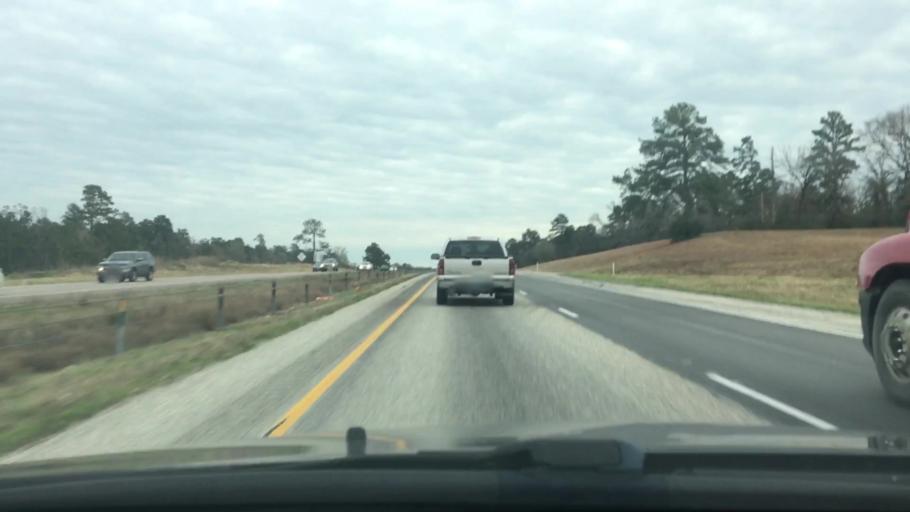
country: US
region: Texas
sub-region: Walker County
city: Huntsville
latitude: 30.7758
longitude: -95.6492
